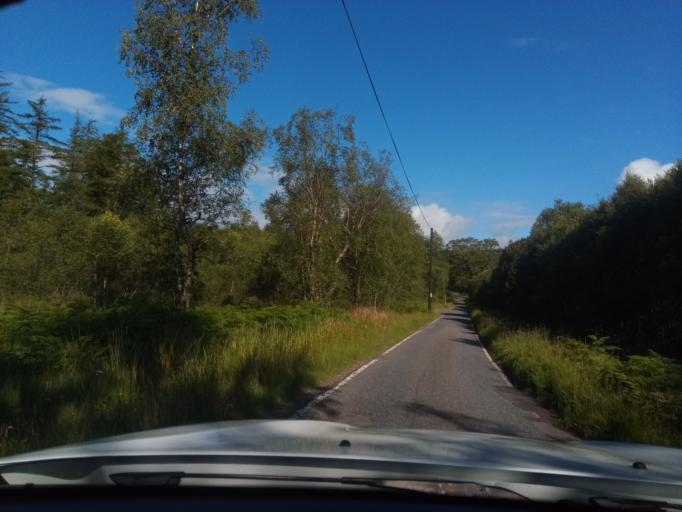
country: GB
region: Scotland
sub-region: Argyll and Bute
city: Isle Of Mull
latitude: 56.6955
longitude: -5.6839
